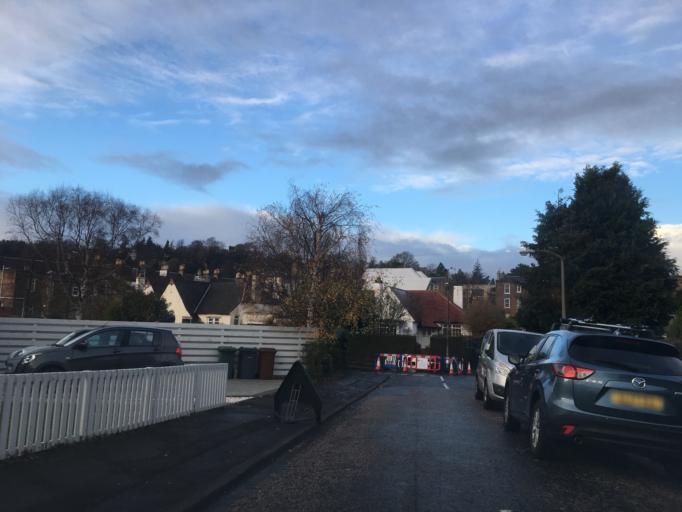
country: GB
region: Scotland
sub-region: Edinburgh
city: Colinton
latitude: 55.9435
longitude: -3.2494
